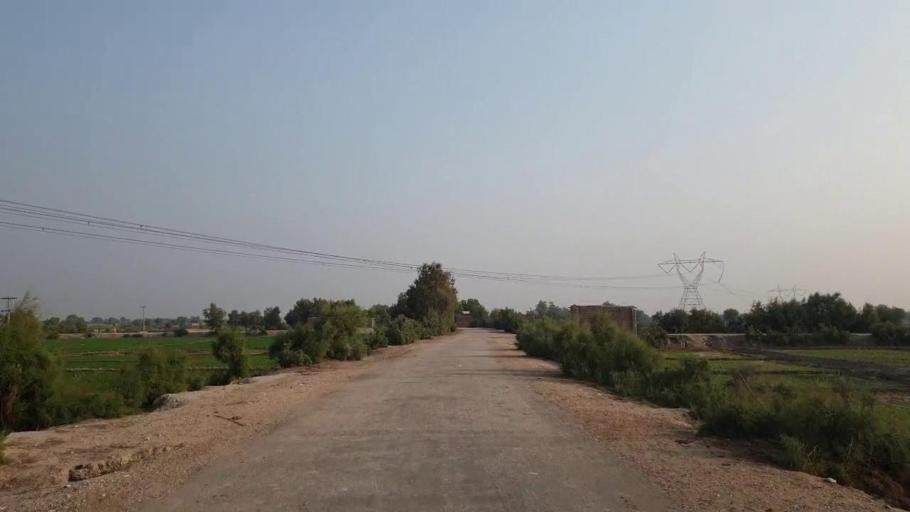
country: PK
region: Sindh
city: Bhan
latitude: 26.4930
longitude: 67.7716
